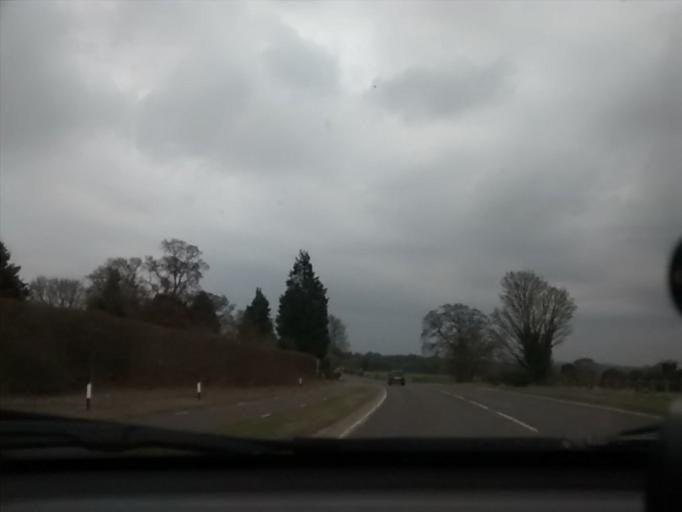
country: GB
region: England
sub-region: Cambridgeshire
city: Sawston
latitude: 52.1487
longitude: 0.1917
